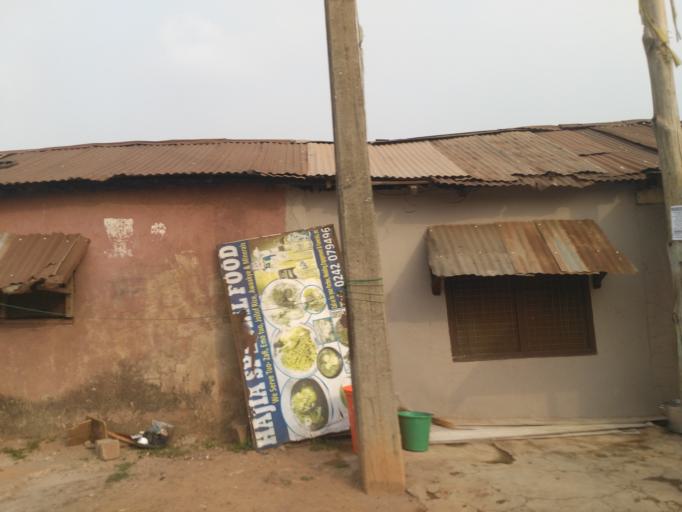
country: GH
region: Ashanti
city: Kumasi
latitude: 6.6945
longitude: -1.6131
